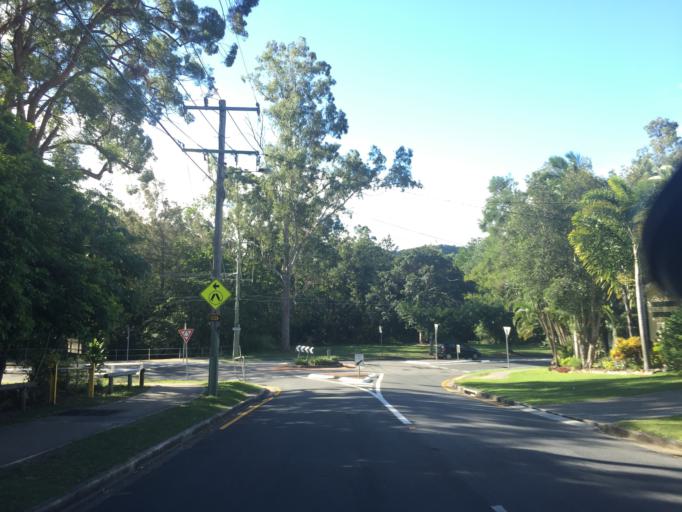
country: AU
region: Queensland
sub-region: Brisbane
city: Taringa
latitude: -27.4497
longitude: 152.9545
